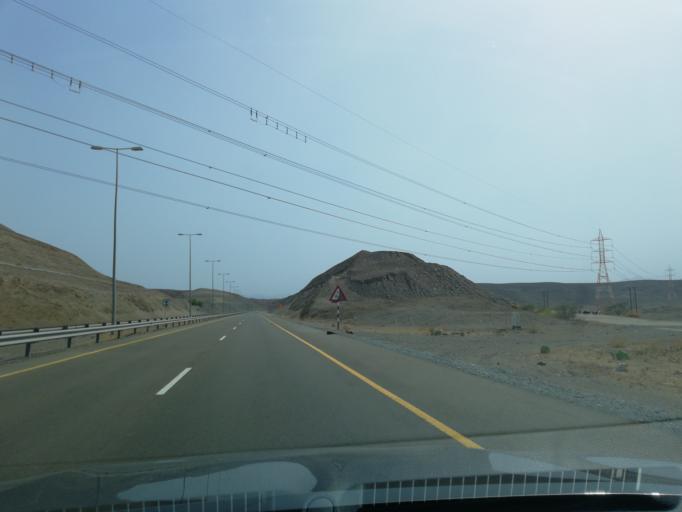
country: OM
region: Al Batinah
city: Al Liwa'
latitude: 24.3124
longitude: 56.4494
